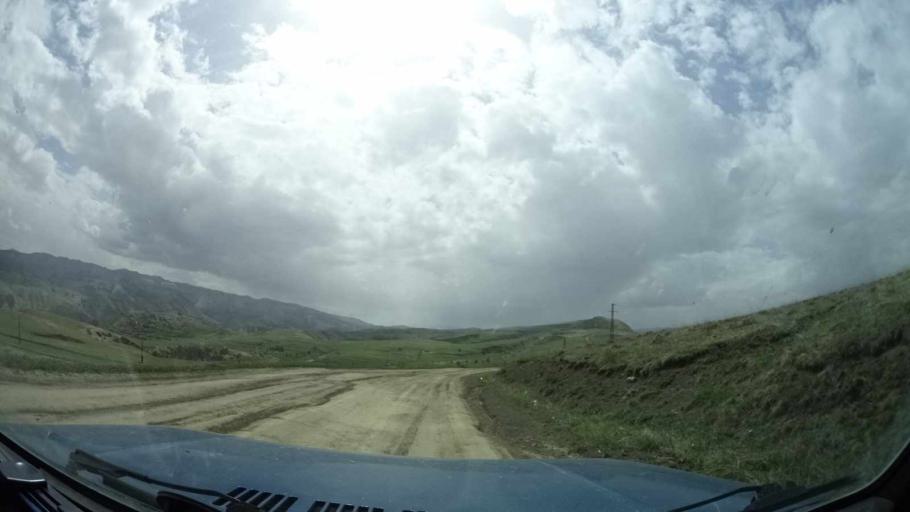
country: RU
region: Dagestan
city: Kubachi
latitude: 42.0807
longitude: 47.5582
